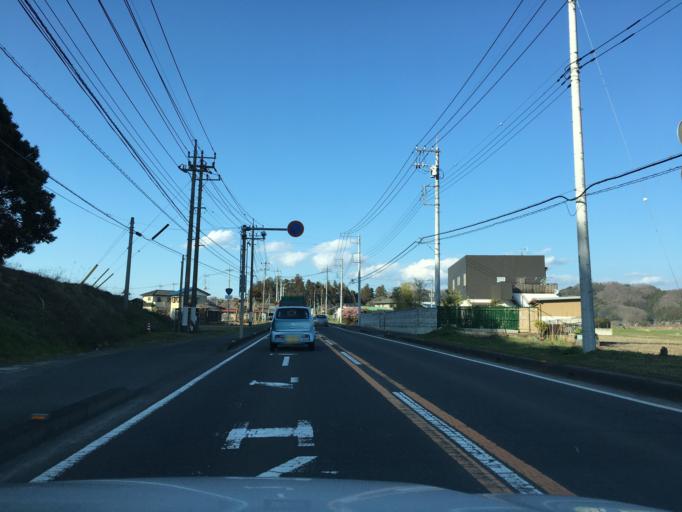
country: JP
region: Ibaraki
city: Omiya
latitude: 36.5906
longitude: 140.4112
